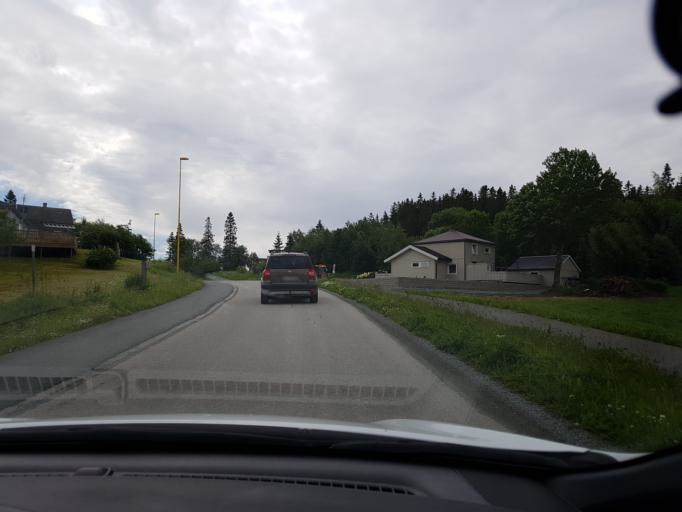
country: NO
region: Nord-Trondelag
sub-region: Frosta
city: Frosta
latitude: 63.5957
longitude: 10.7362
